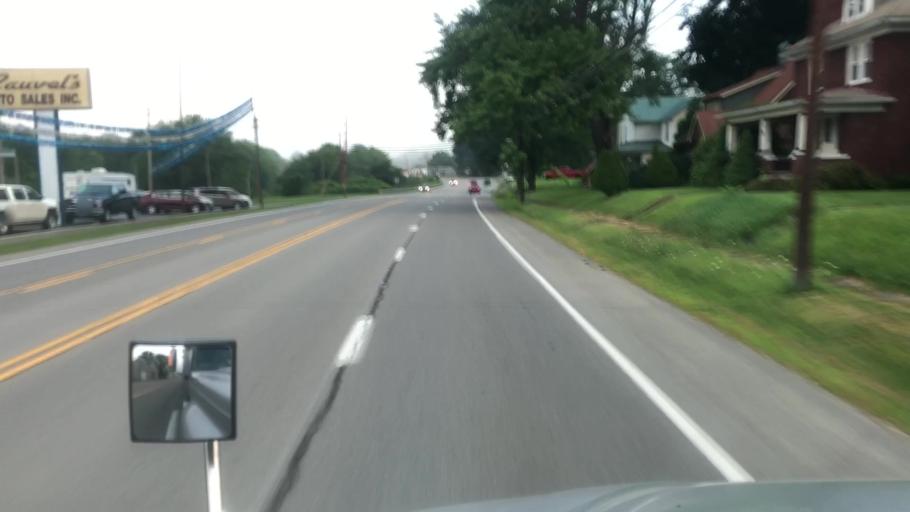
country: US
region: Pennsylvania
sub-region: Venango County
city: Woodland Heights
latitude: 41.4110
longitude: -79.7546
